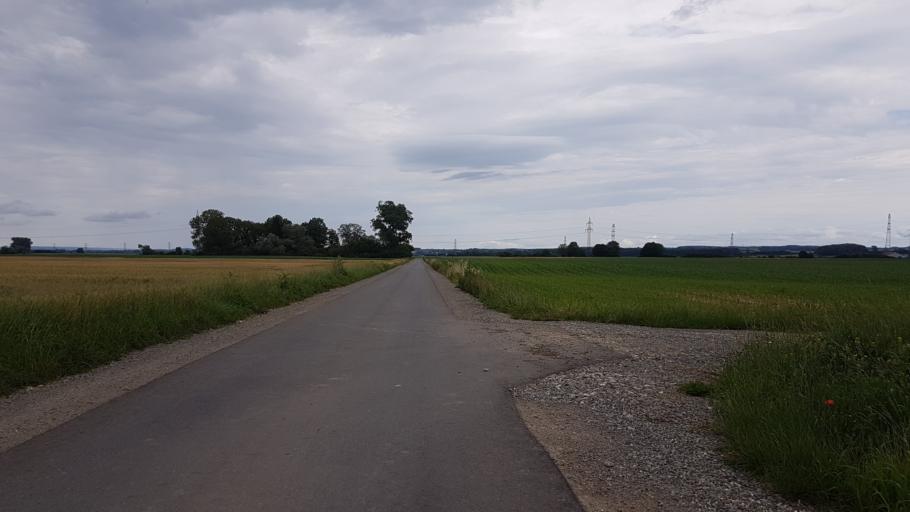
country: DE
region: Baden-Wuerttemberg
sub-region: Tuebingen Region
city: Herbertingen
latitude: 48.0745
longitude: 9.4076
